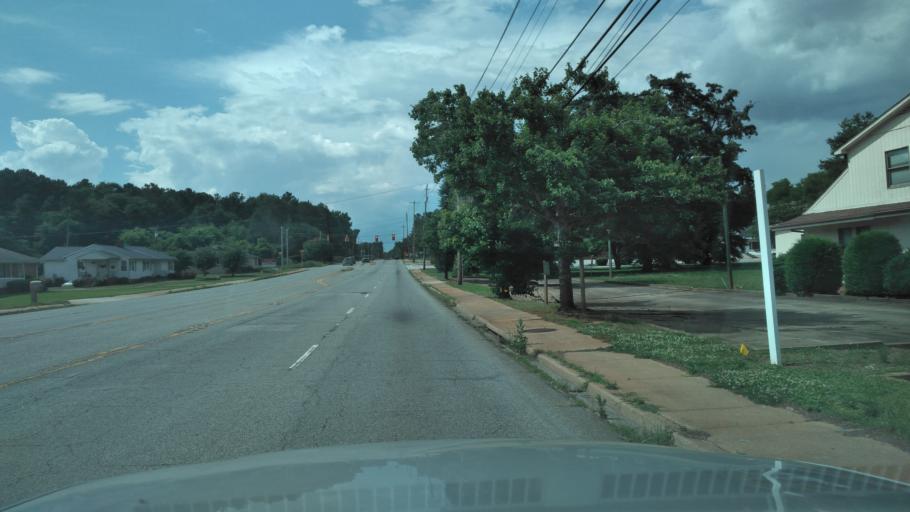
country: US
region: South Carolina
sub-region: Spartanburg County
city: Saxon
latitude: 34.9786
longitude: -81.9431
